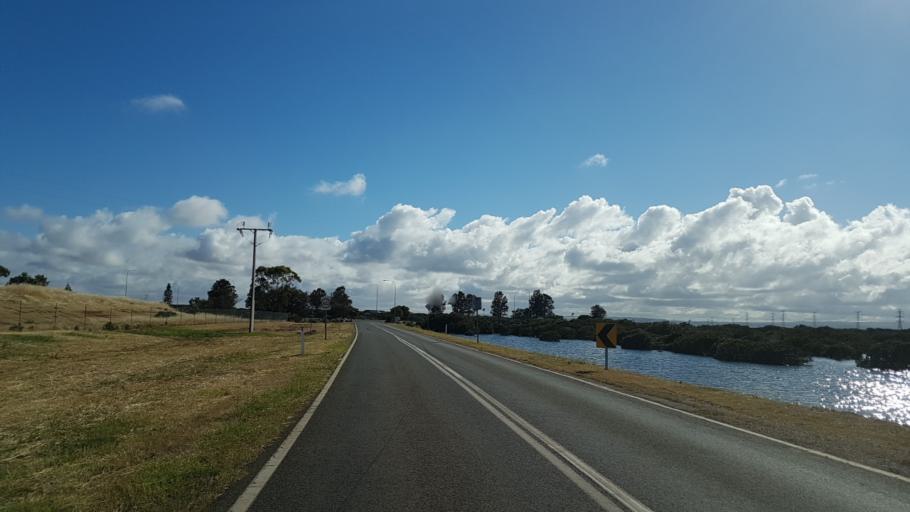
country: AU
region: South Australia
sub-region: Port Adelaide Enfield
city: Birkenhead
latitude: -34.8071
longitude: 138.5385
